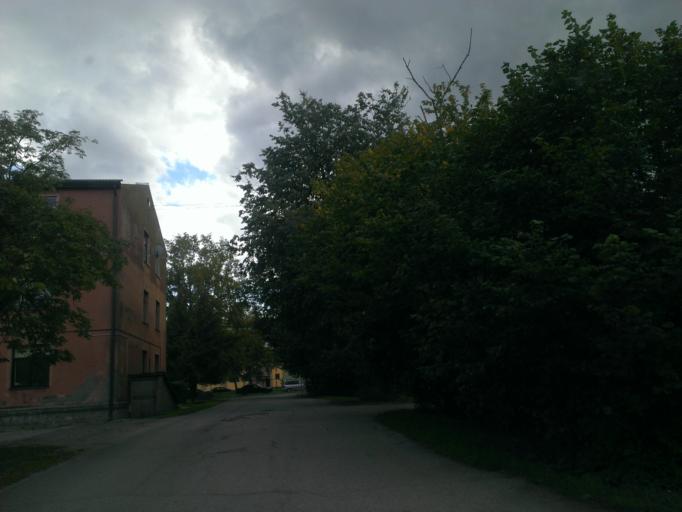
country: LV
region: Sigulda
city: Sigulda
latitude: 57.1539
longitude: 24.8796
